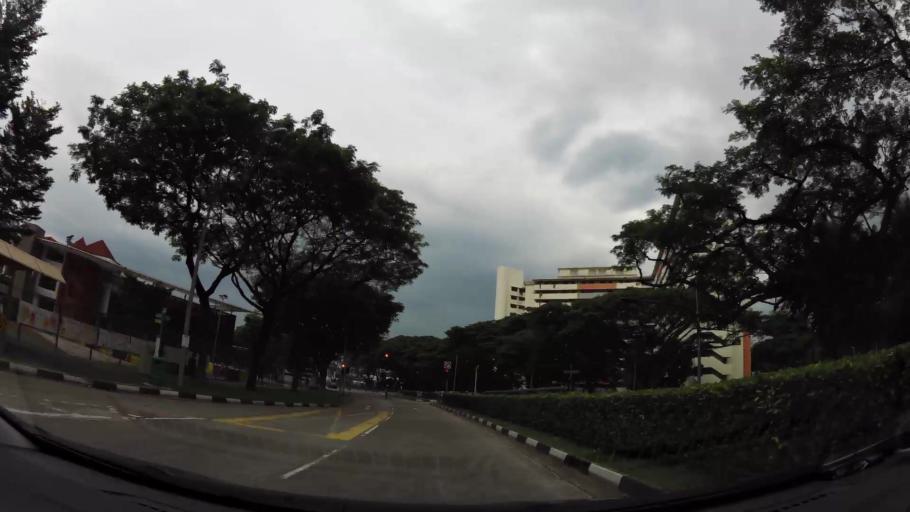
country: SG
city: Singapore
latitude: 1.3149
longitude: 103.8728
